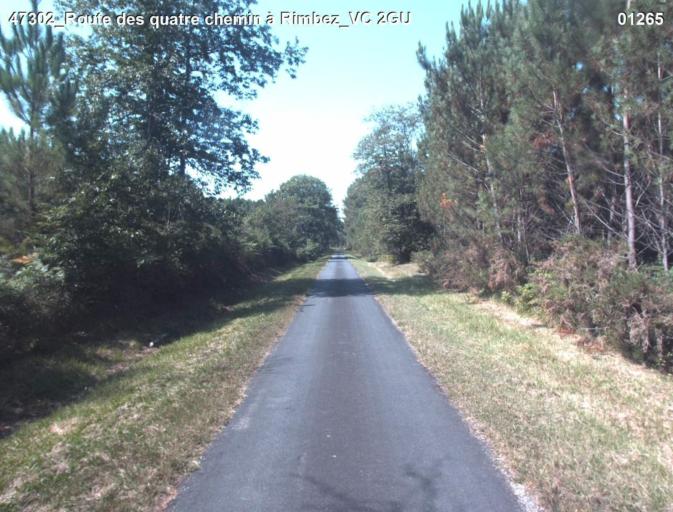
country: FR
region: Aquitaine
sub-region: Departement des Landes
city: Gabarret
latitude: 44.0326
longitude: 0.0801
